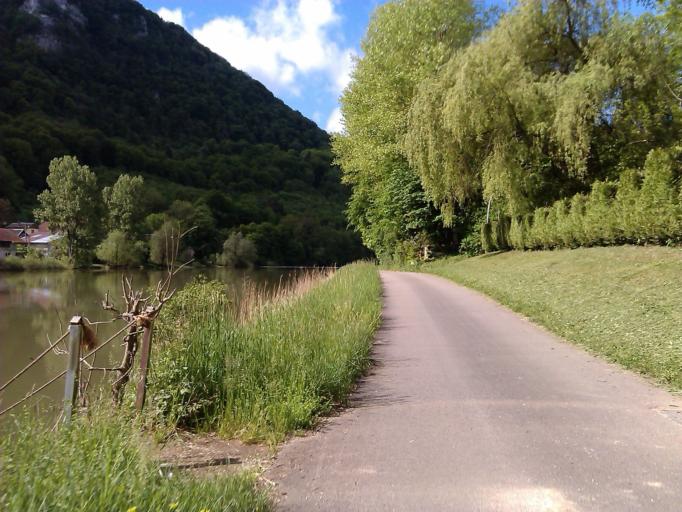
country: FR
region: Franche-Comte
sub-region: Departement du Doubs
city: Roulans
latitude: 47.3231
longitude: 6.2842
